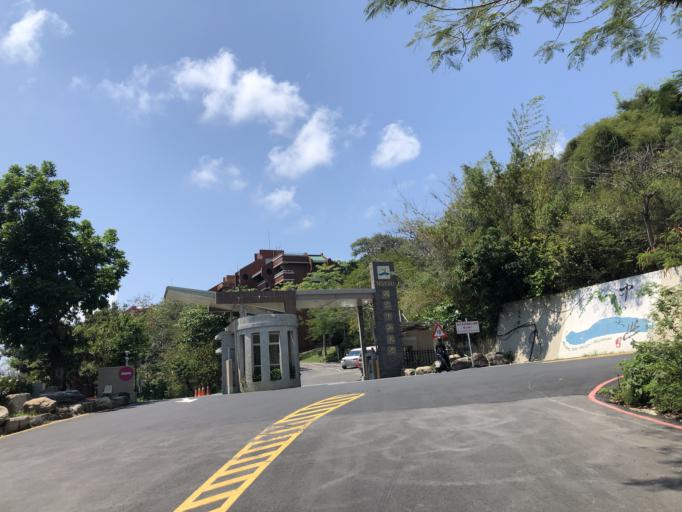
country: TW
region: Kaohsiung
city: Kaohsiung
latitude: 22.6266
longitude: 120.2711
